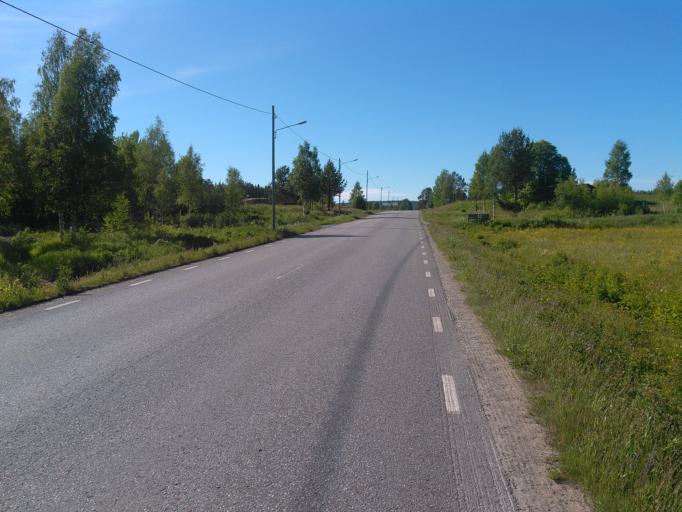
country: SE
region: Vaesterbotten
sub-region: Umea Kommun
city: Roback
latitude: 63.8259
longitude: 20.1217
